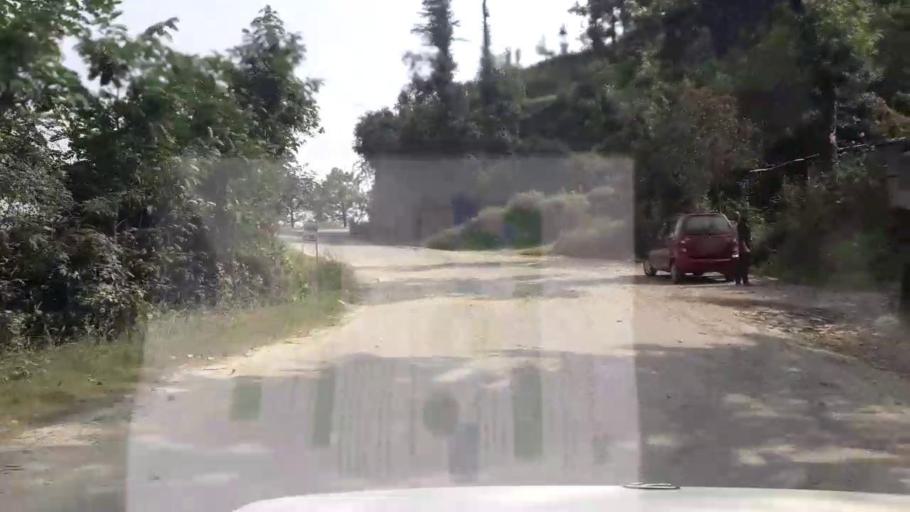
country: IN
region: Himachal Pradesh
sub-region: Shimla
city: Shimla
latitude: 31.0594
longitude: 77.1553
